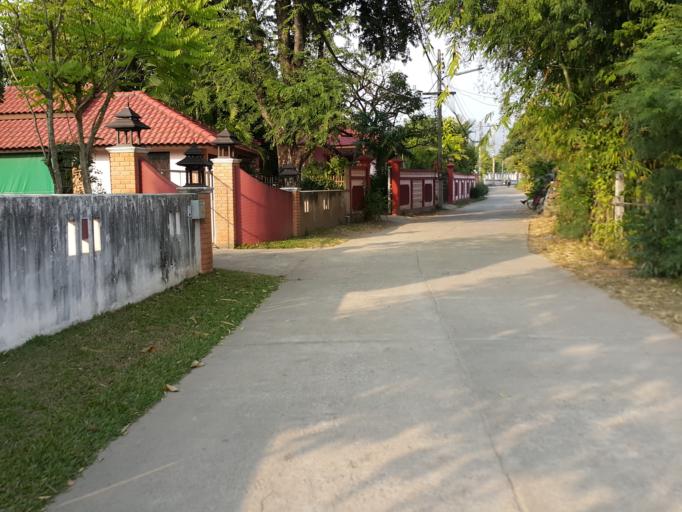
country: TH
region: Chiang Mai
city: San Sai
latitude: 18.8829
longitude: 99.1450
